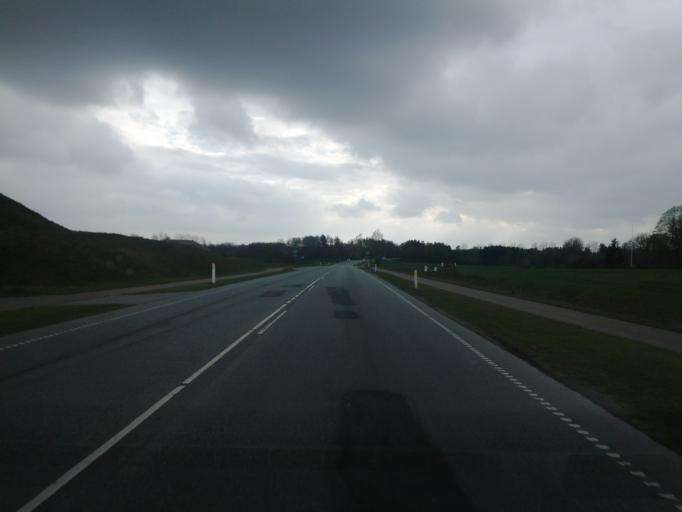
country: DK
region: North Denmark
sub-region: Frederikshavn Kommune
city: Saeby
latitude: 57.3200
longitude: 10.4784
